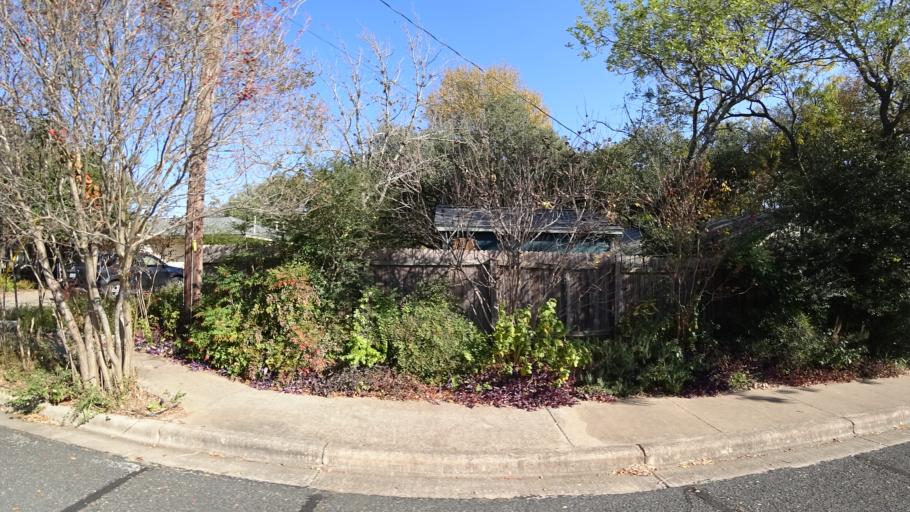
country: US
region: Texas
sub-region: Travis County
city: Barton Creek
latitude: 30.2267
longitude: -97.8485
